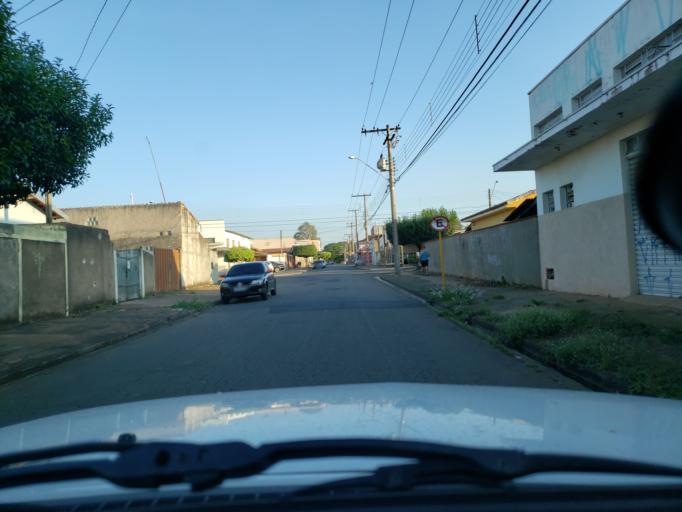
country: BR
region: Sao Paulo
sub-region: Moji-Guacu
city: Mogi-Gaucu
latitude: -22.3437
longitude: -46.9384
